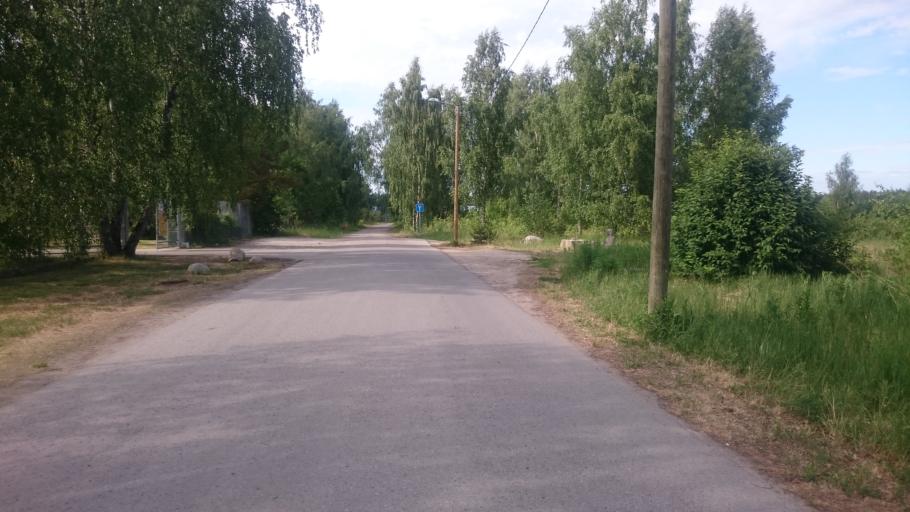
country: EE
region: Harju
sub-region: Tallinna linn
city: Tallinn
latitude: 59.3719
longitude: 24.7429
